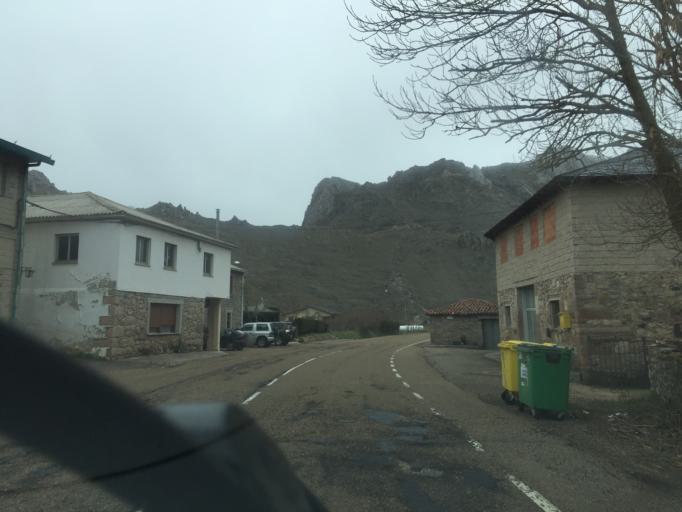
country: ES
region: Castille and Leon
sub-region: Provincia de Leon
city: Sena de Luna
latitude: 42.9427
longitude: -5.9829
